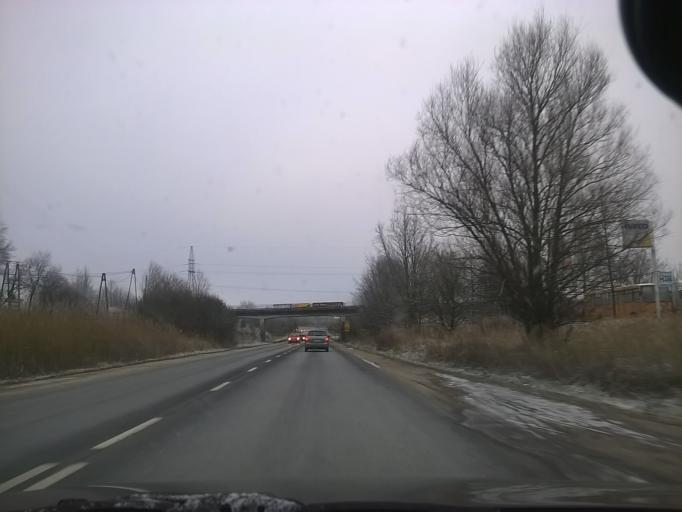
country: PL
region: Warmian-Masurian Voivodeship
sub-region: Powiat olsztynski
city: Olsztyn
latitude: 53.7819
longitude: 20.5460
